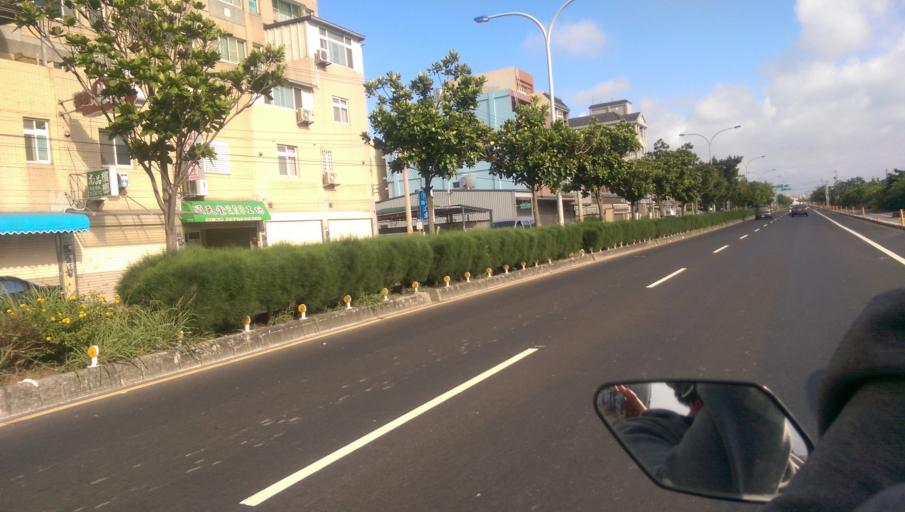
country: TW
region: Taiwan
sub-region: Hsinchu
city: Hsinchu
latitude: 24.8386
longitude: 120.9354
